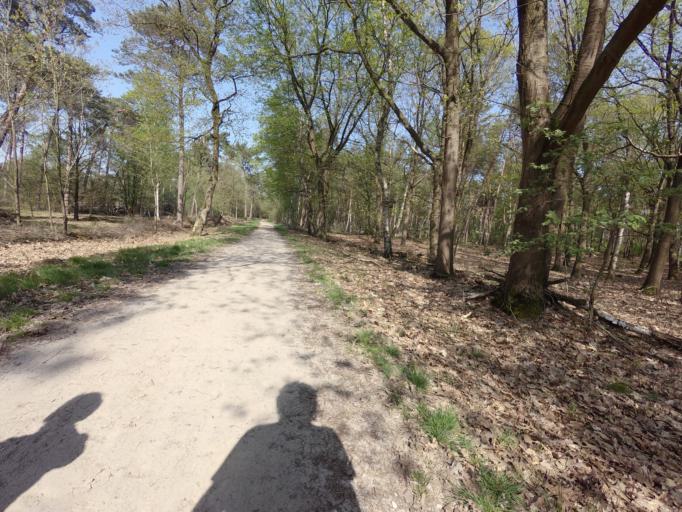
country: NL
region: North Brabant
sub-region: Gemeente Goirle
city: Goirle
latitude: 51.4992
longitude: 5.0101
